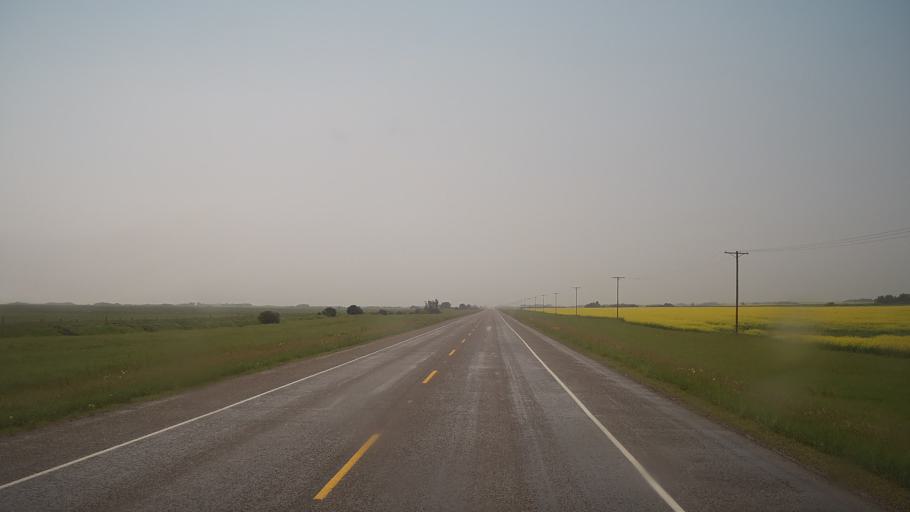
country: CA
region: Saskatchewan
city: Biggar
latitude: 52.1479
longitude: -108.2185
